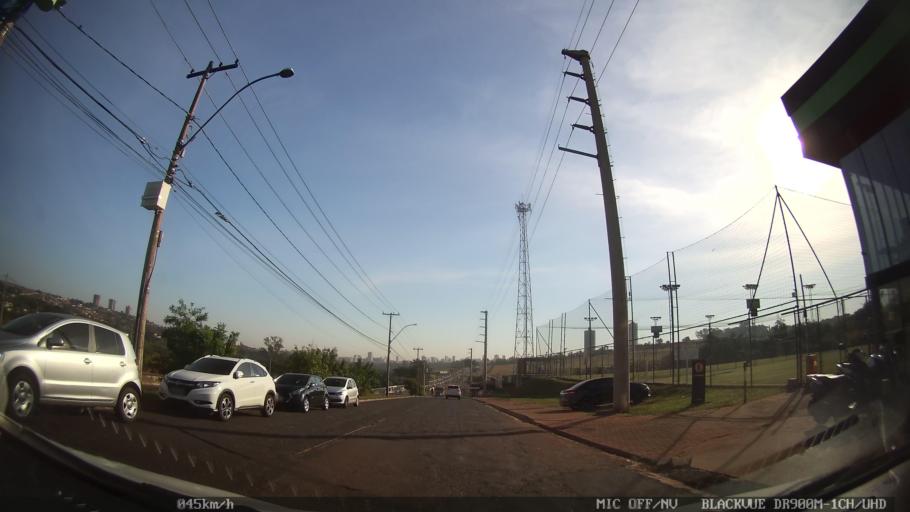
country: BR
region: Sao Paulo
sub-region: Ribeirao Preto
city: Ribeirao Preto
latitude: -21.2514
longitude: -47.8190
